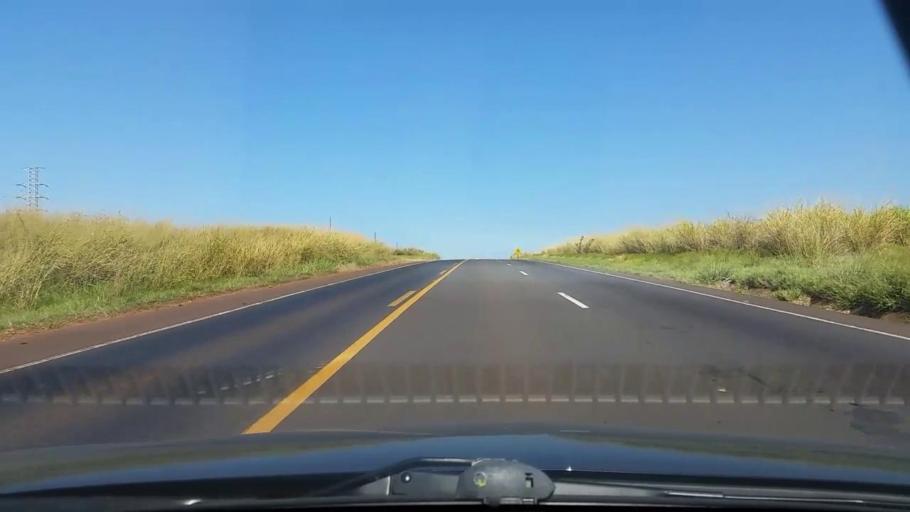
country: BR
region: Sao Paulo
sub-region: Jau
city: Jau
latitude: -22.3533
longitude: -48.5725
